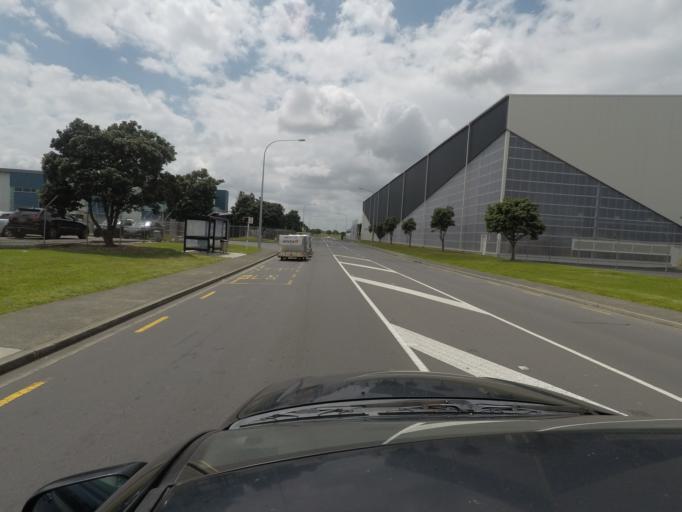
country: NZ
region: Auckland
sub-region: Auckland
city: Mangere
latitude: -37.0017
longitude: 174.7964
